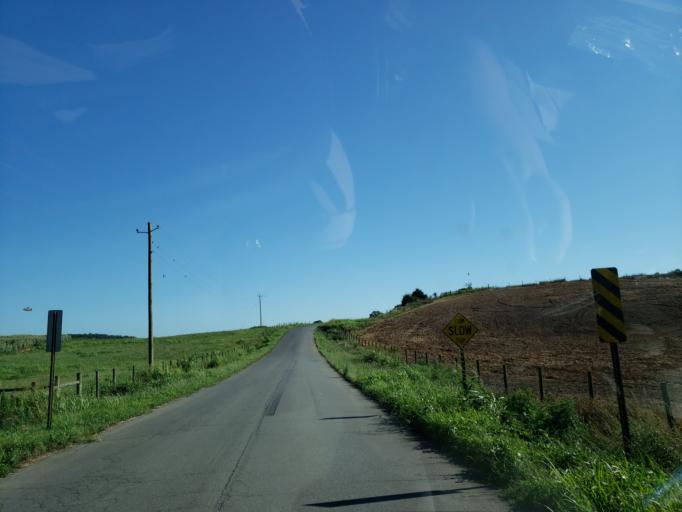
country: US
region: Georgia
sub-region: Bartow County
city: Euharlee
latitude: 34.0991
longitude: -84.9018
